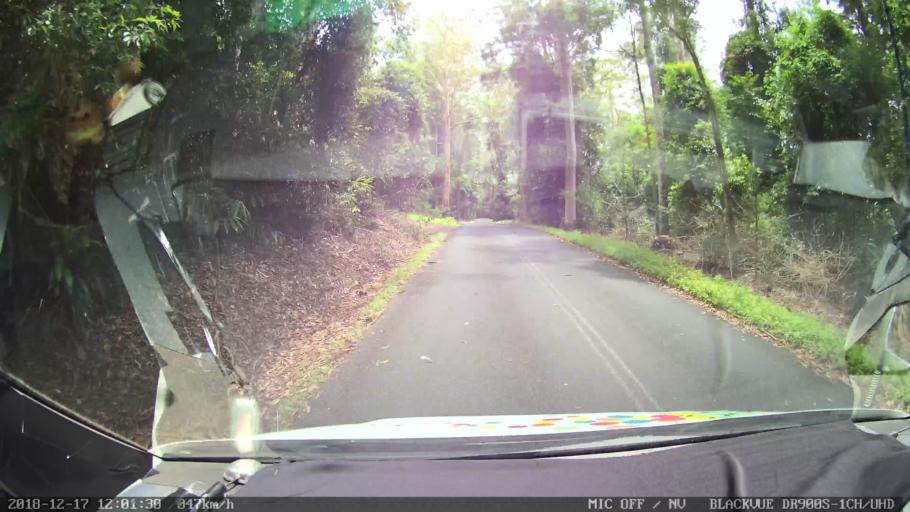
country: AU
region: New South Wales
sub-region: Kyogle
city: Kyogle
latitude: -28.5214
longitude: 152.5712
